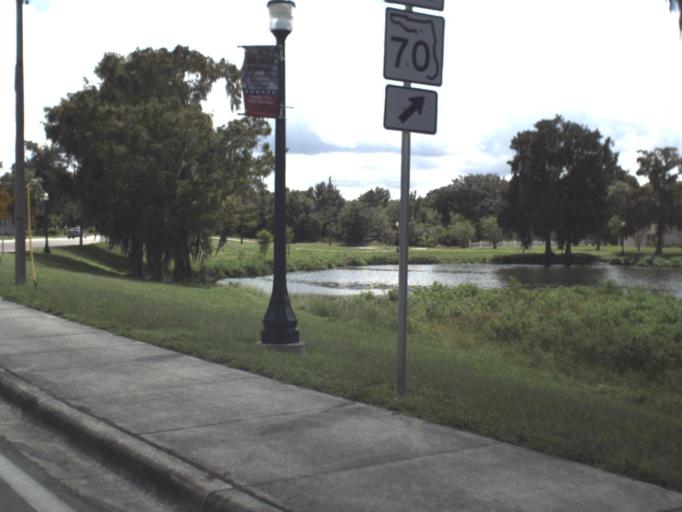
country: US
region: Florida
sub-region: DeSoto County
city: Arcadia
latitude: 27.2194
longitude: -81.8719
